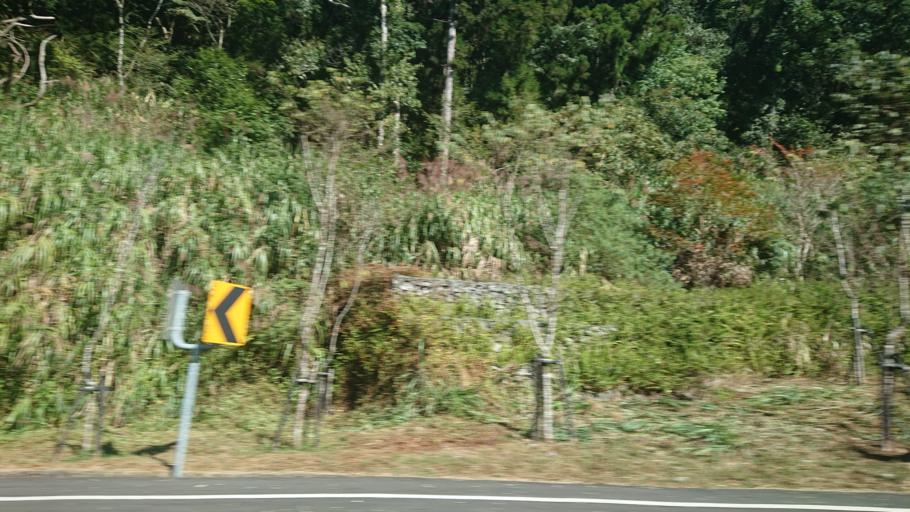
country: TW
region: Taiwan
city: Lugu
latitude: 23.4977
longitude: 120.7816
